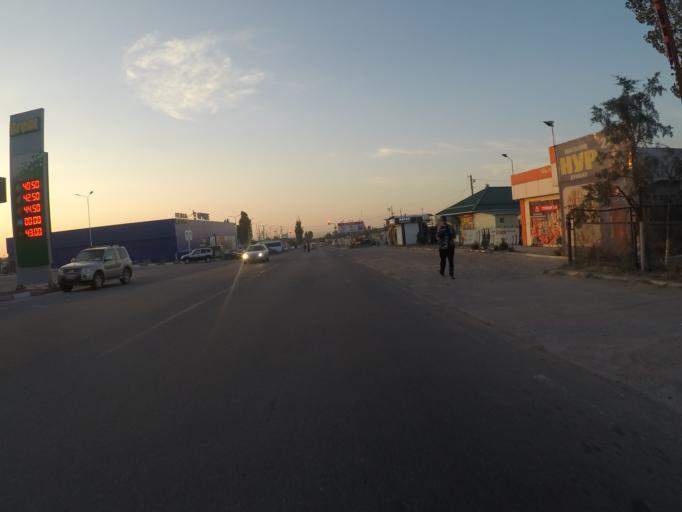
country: KG
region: Chuy
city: Lebedinovka
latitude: 42.8021
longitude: 74.6489
